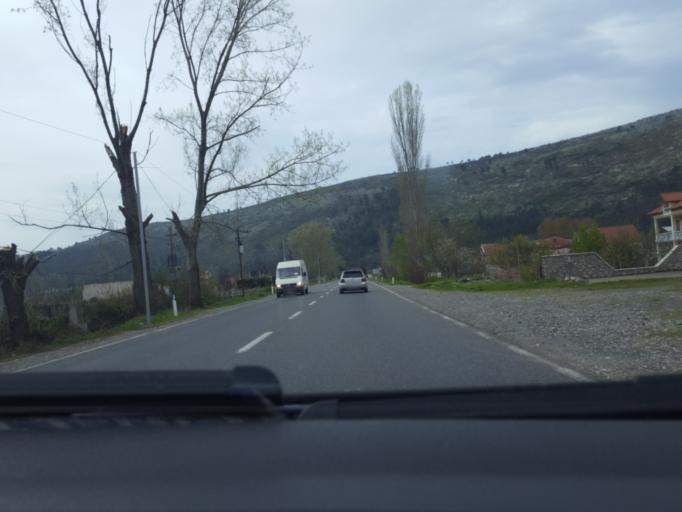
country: AL
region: Lezhe
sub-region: Rrethi i Lezhes
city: Balldreni i Ri
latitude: 41.8079
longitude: 19.6337
